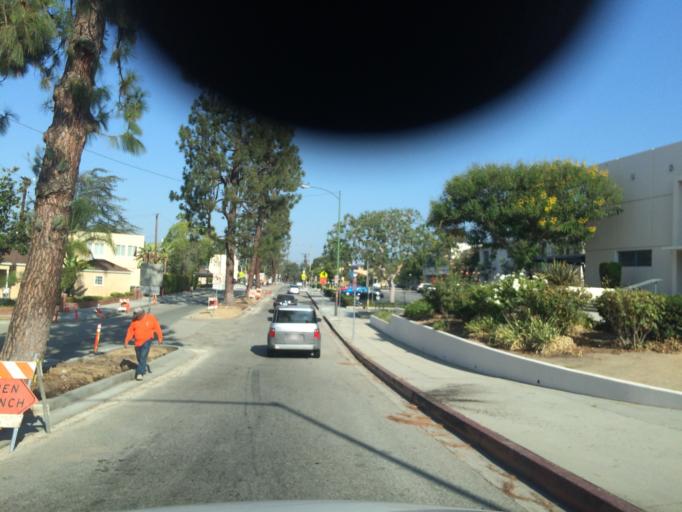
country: US
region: California
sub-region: Los Angeles County
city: Glendale
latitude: 34.1550
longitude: -118.2377
